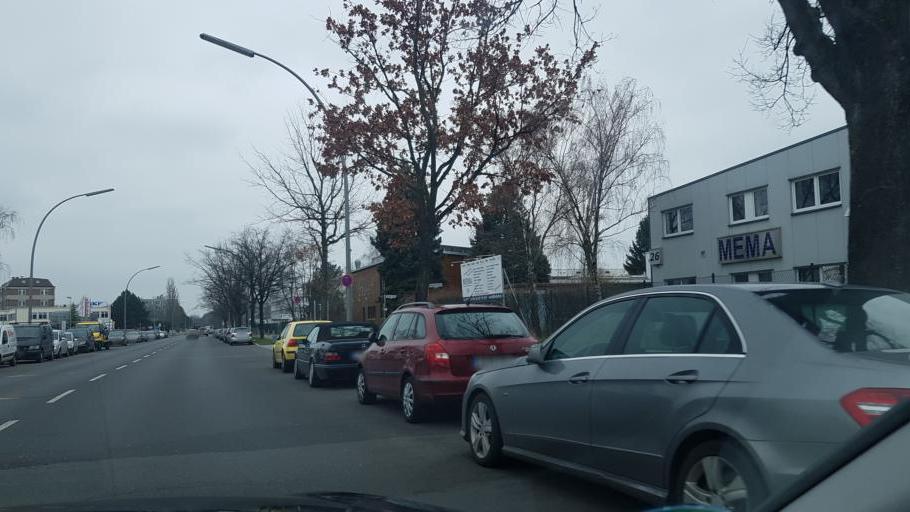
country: DE
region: Berlin
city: Marienfelde
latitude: 52.4034
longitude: 13.3828
